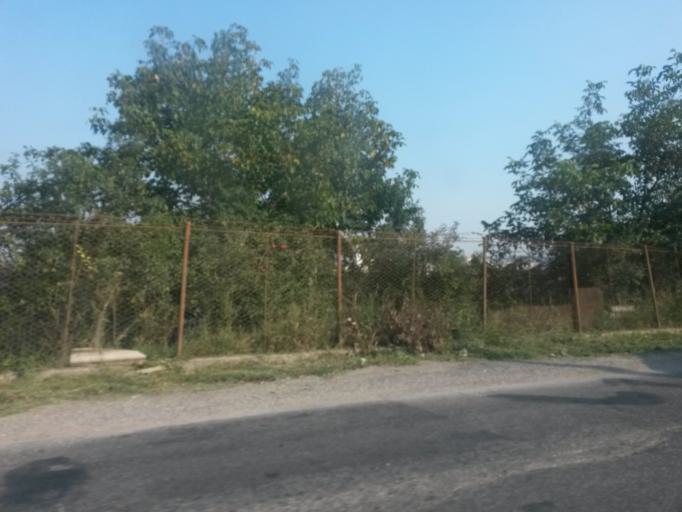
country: RO
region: Cluj
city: Turda
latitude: 46.5627
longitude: 23.7752
